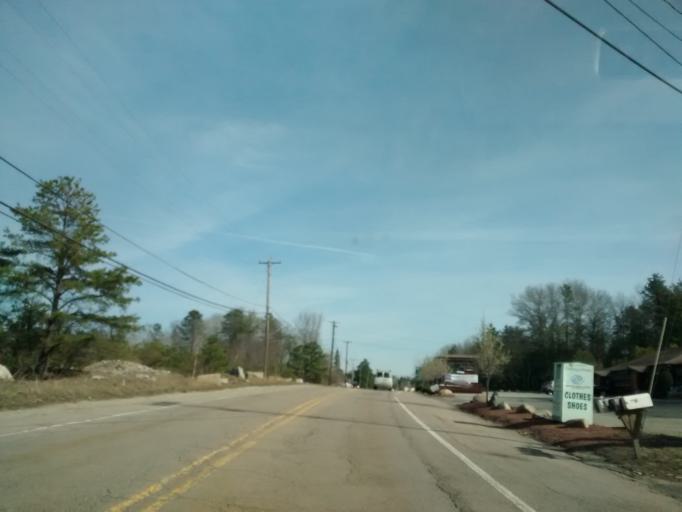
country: US
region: Massachusetts
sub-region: Worcester County
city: Millville
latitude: 42.0280
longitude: -71.6065
